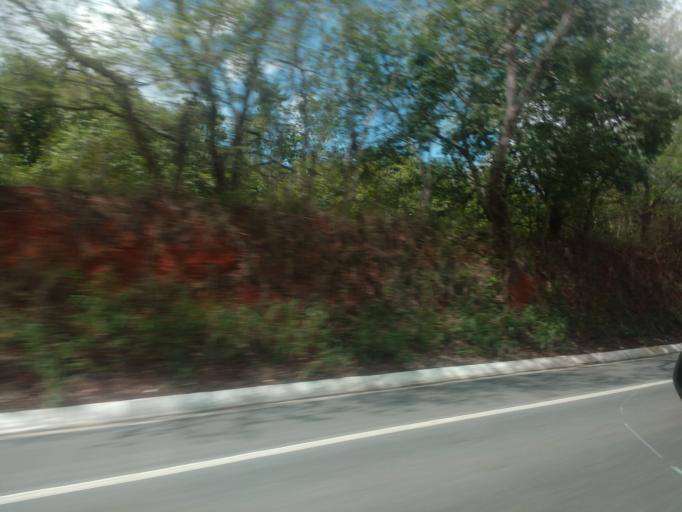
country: BR
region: Alagoas
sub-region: Murici
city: Murici
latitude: -9.2619
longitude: -35.9873
